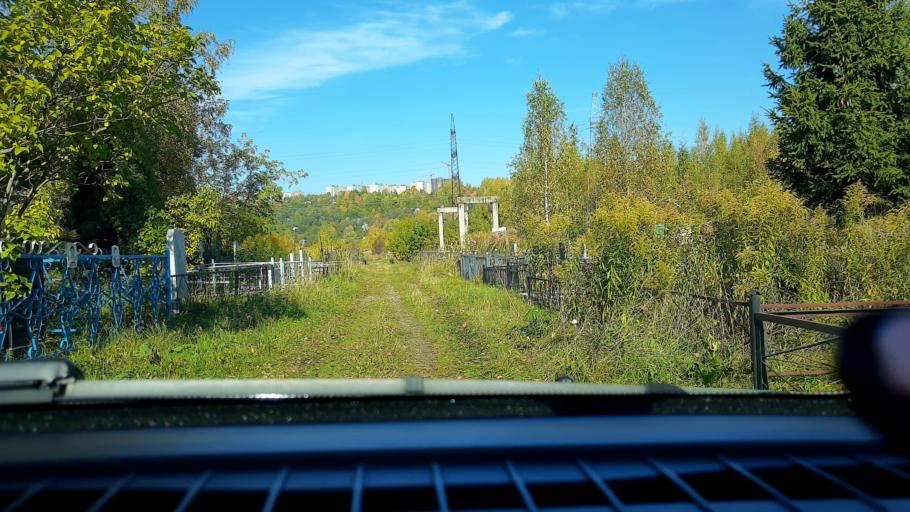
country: RU
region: Nizjnij Novgorod
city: Afonino
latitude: 56.2350
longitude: 44.0628
